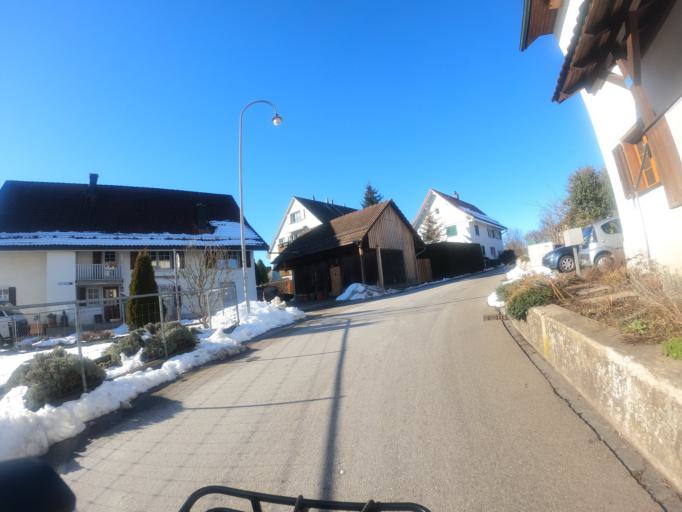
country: CH
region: Zurich
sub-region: Bezirk Affoltern
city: Ottenbach
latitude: 47.2817
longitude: 8.4001
